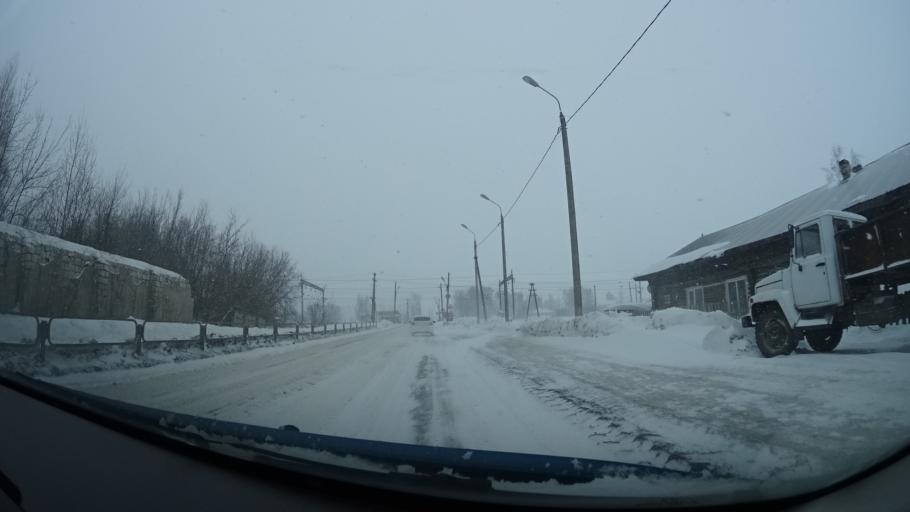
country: RU
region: Perm
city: Kuyeda
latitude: 56.4255
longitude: 55.5814
